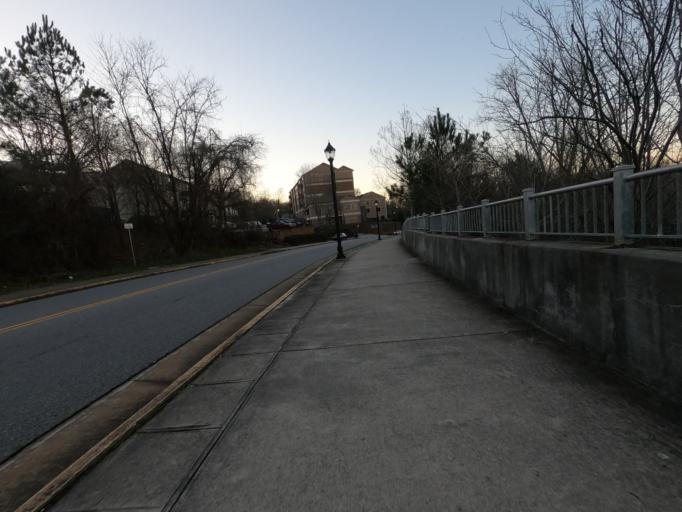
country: US
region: Georgia
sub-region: Clarke County
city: Athens
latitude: 33.9629
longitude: -83.3707
